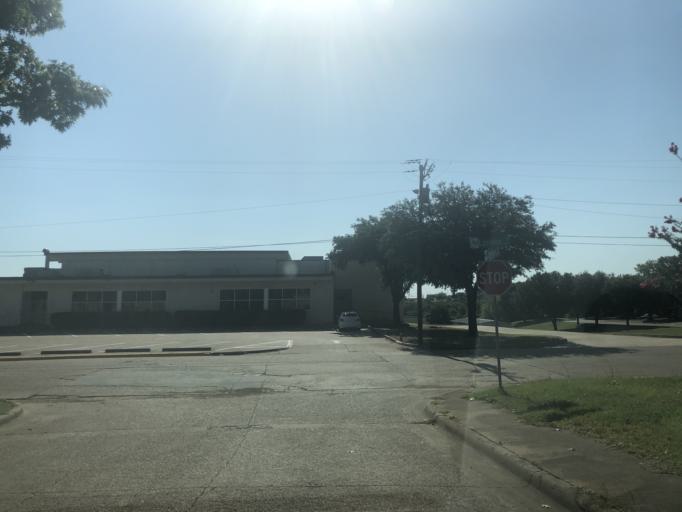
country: US
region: Texas
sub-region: Dallas County
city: Grand Prairie
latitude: 32.7575
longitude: -97.0184
